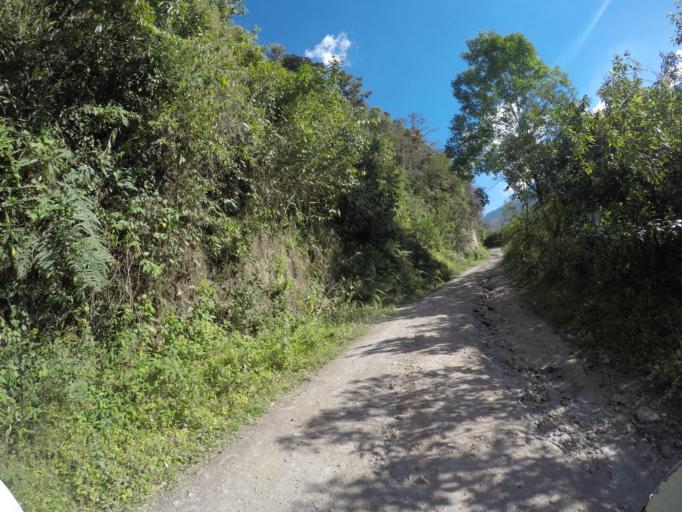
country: CO
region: Tolima
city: Cajamarca
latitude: 4.5179
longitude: -75.4067
